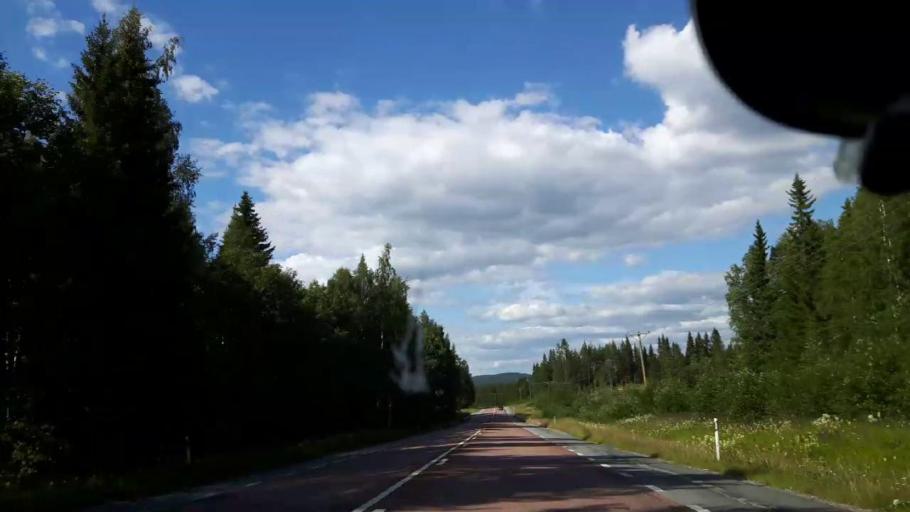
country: SE
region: Jaemtland
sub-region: Braecke Kommun
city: Braecke
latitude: 62.8038
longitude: 15.3701
